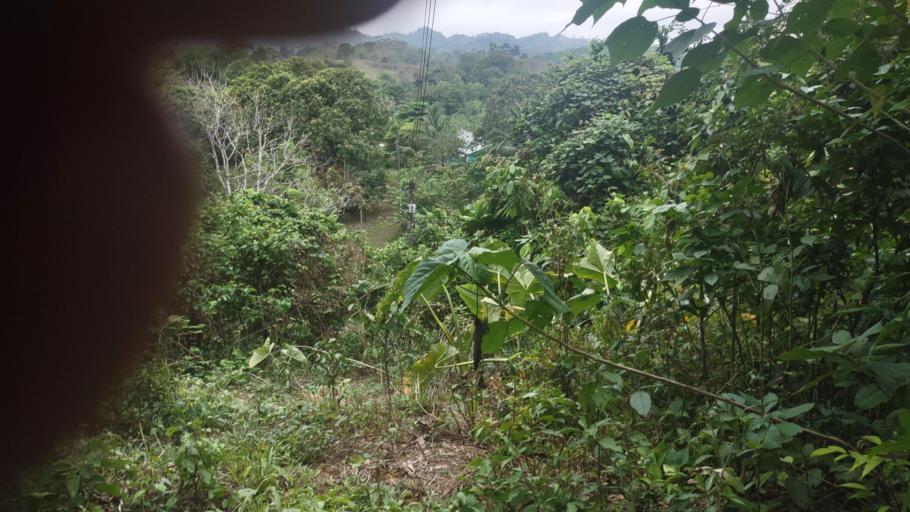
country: MX
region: Veracruz
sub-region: Uxpanapa
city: Poblado 10
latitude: 17.4728
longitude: -94.1225
